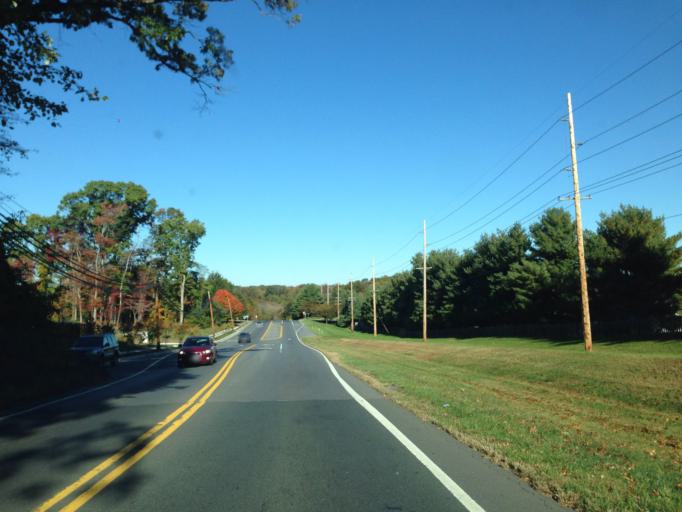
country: US
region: Maryland
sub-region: Montgomery County
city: Clarksburg
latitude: 39.2181
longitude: -77.2552
